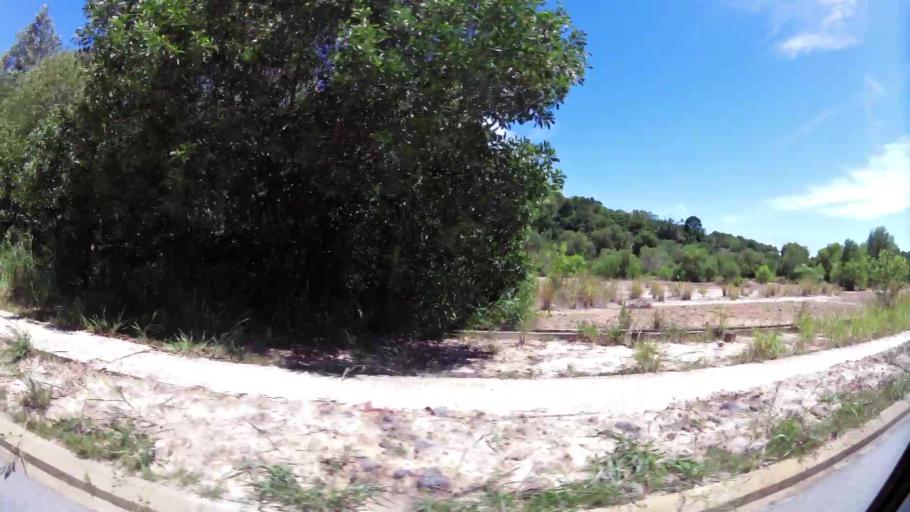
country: BN
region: Brunei and Muara
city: Bandar Seri Begawan
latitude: 5.0344
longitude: 115.0367
